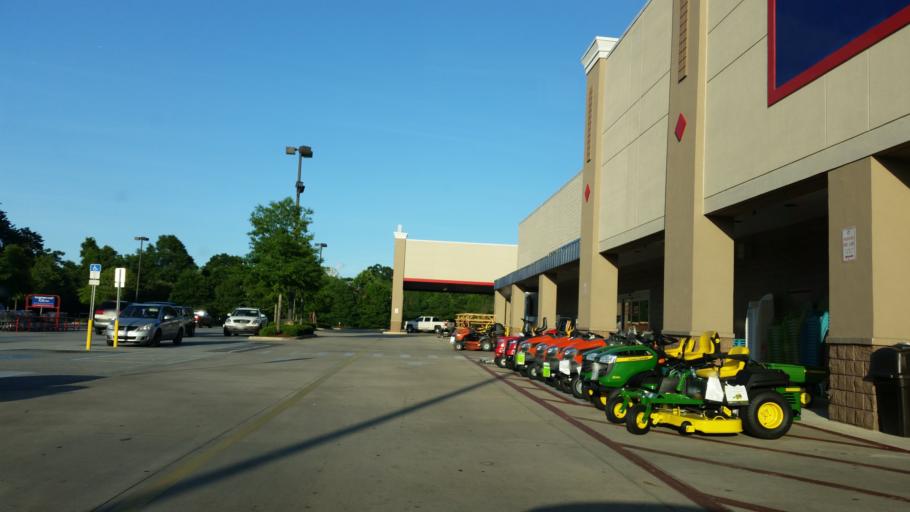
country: US
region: Florida
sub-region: Santa Rosa County
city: Pace
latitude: 30.6014
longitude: -87.1095
